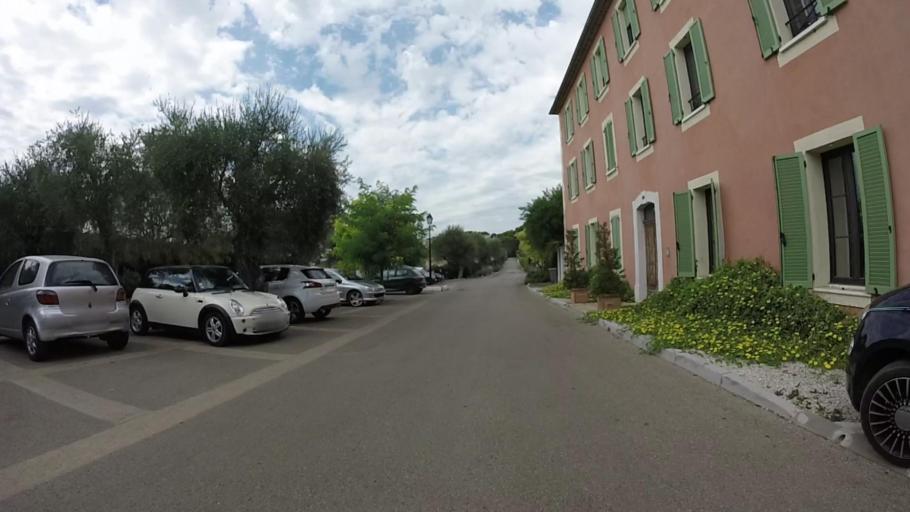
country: FR
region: Provence-Alpes-Cote d'Azur
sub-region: Departement des Alpes-Maritimes
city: Biot
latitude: 43.6196
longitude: 7.0872
